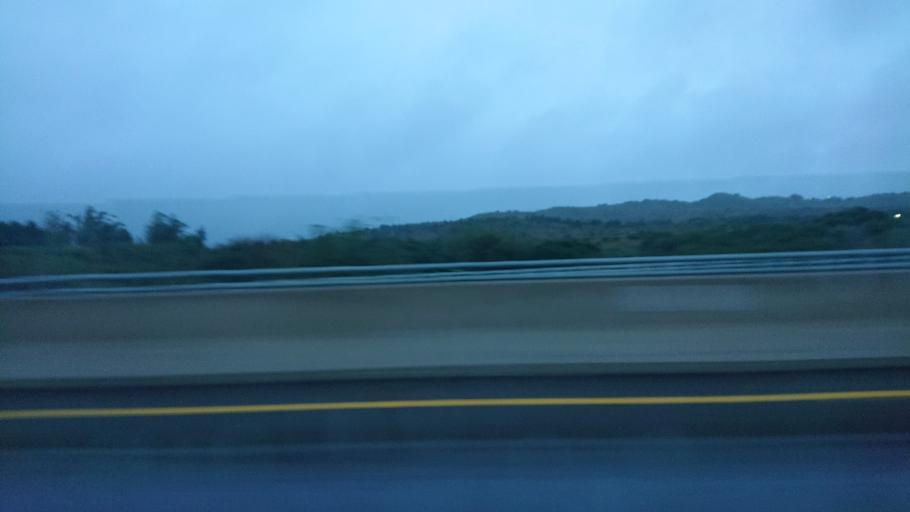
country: TW
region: Taiwan
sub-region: Miaoli
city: Miaoli
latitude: 24.5520
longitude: 120.7075
